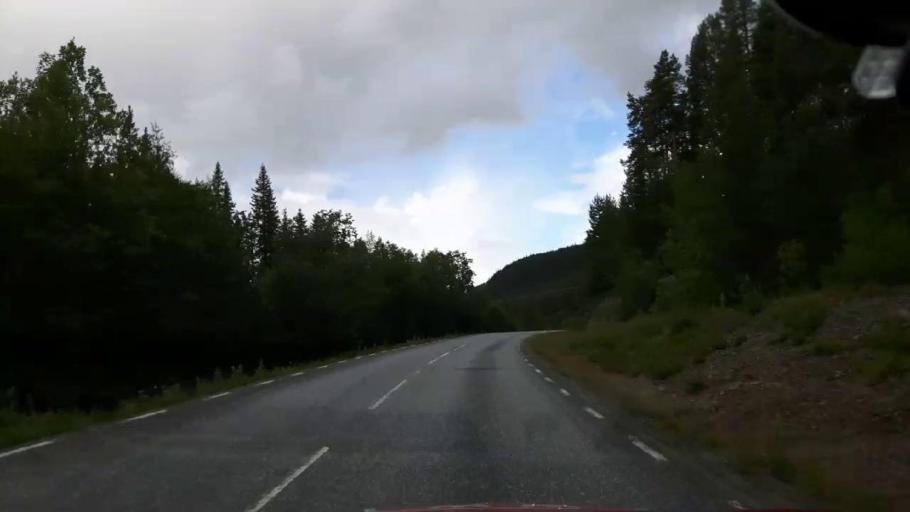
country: SE
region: Vaesterbotten
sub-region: Vilhelmina Kommun
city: Sjoberg
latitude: 64.9422
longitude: 15.8332
